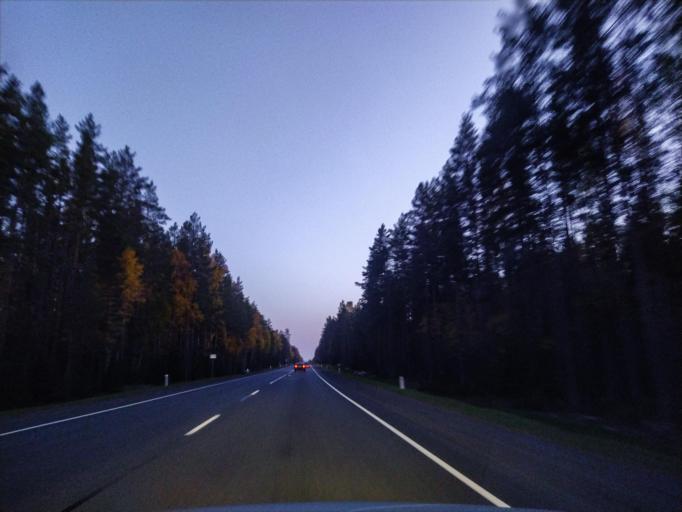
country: RU
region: Leningrad
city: Priozersk
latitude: 60.9048
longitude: 30.1602
